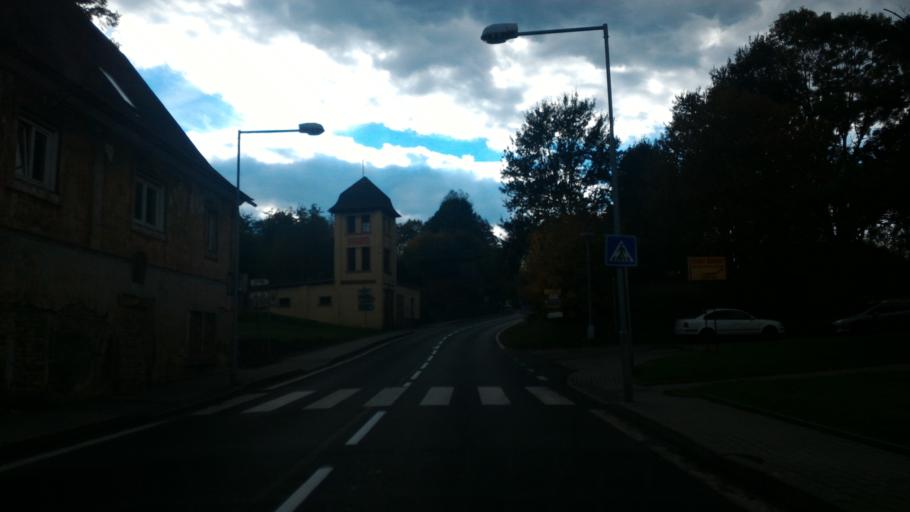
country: CZ
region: Ustecky
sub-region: Okres Decin
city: Chribska
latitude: 50.8625
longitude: 14.4812
